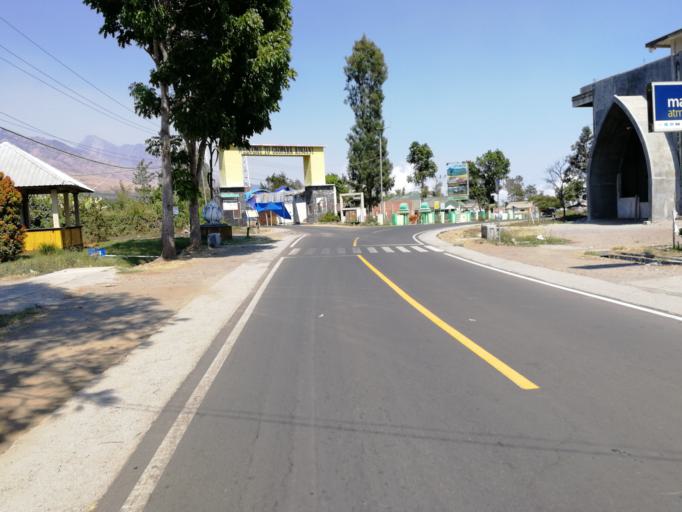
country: ID
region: West Nusa Tenggara
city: Sembalunlawang
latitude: -8.3599
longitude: 116.5250
